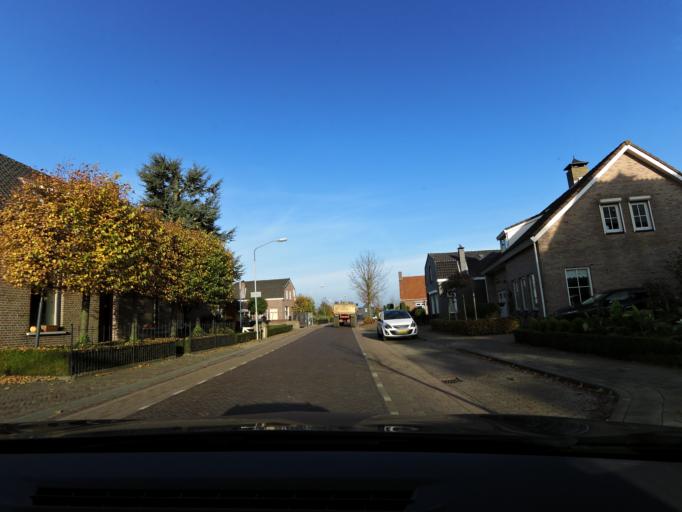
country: NL
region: North Brabant
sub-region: Gemeente Made en Drimmelen
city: Made
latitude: 51.6852
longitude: 4.7954
